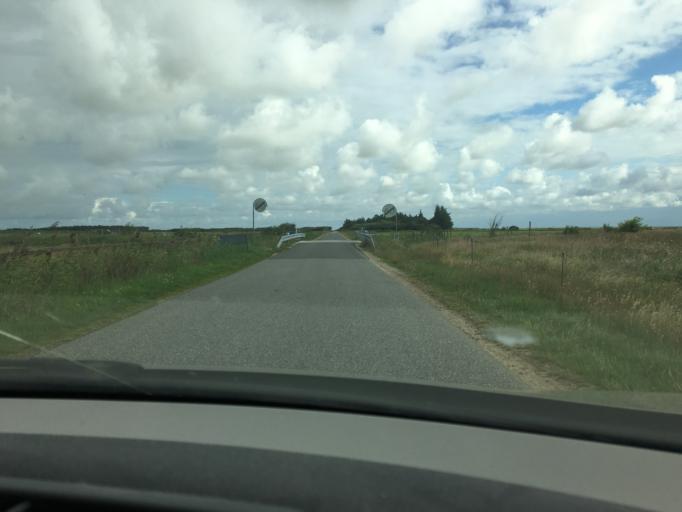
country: DK
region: Central Jutland
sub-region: Ringkobing-Skjern Kommune
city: Hvide Sande
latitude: 55.8284
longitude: 8.2160
